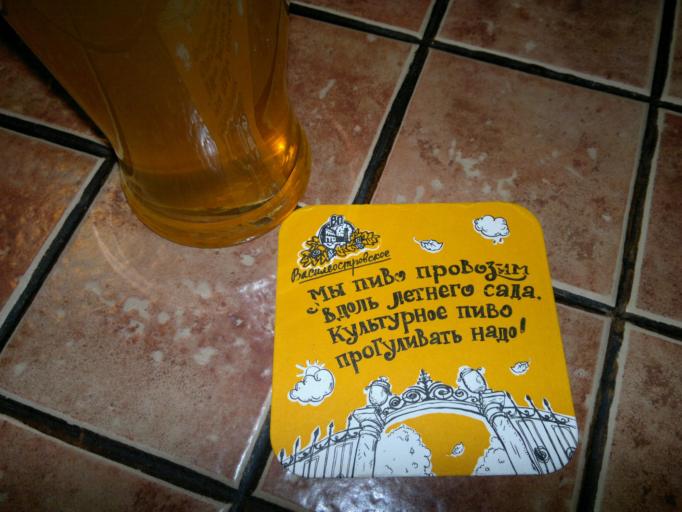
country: RU
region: St.-Petersburg
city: Centralniy
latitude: 59.9245
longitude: 30.3835
